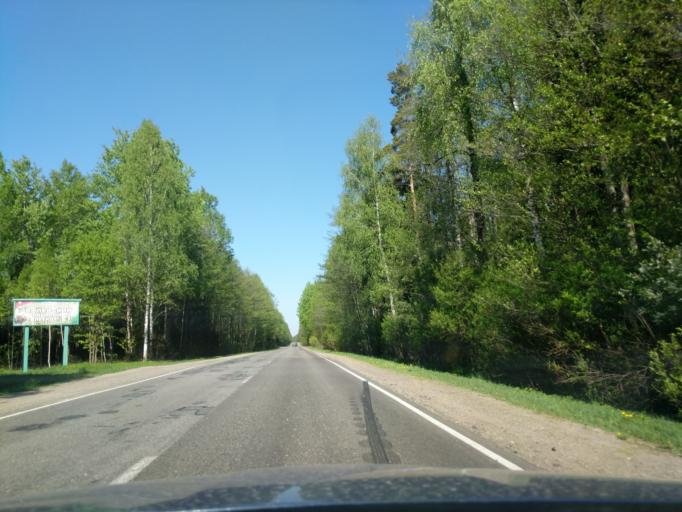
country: BY
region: Minsk
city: Il'ya
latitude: 54.4016
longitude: 27.3260
